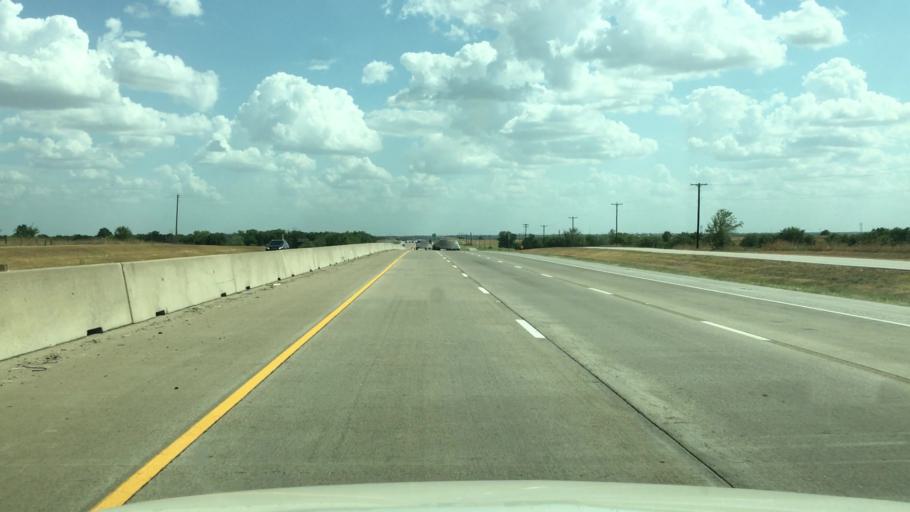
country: US
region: Texas
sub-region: Ellis County
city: Nash
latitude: 32.2745
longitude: -96.8700
